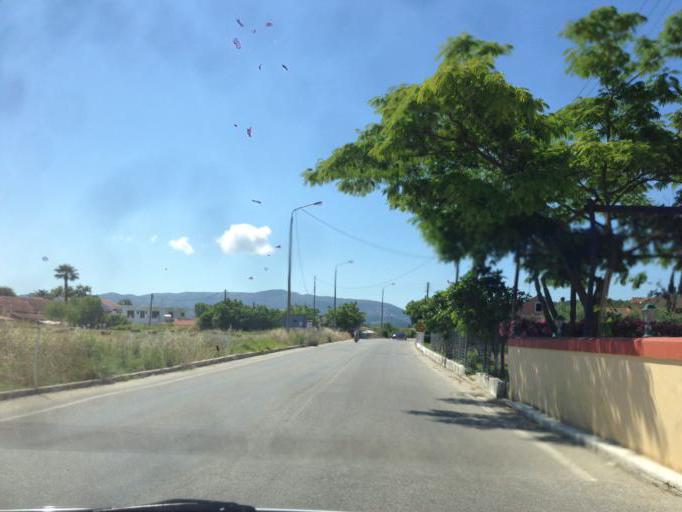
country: GR
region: Ionian Islands
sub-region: Nomos Kerkyras
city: Agios Georgis
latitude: 39.7756
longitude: 19.7117
